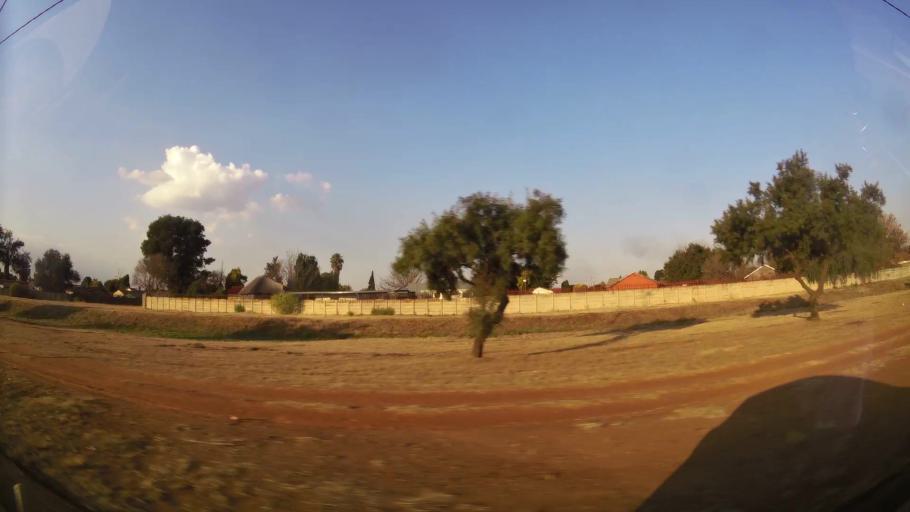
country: ZA
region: Gauteng
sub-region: Ekurhuleni Metropolitan Municipality
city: Germiston
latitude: -26.2812
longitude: 28.2268
